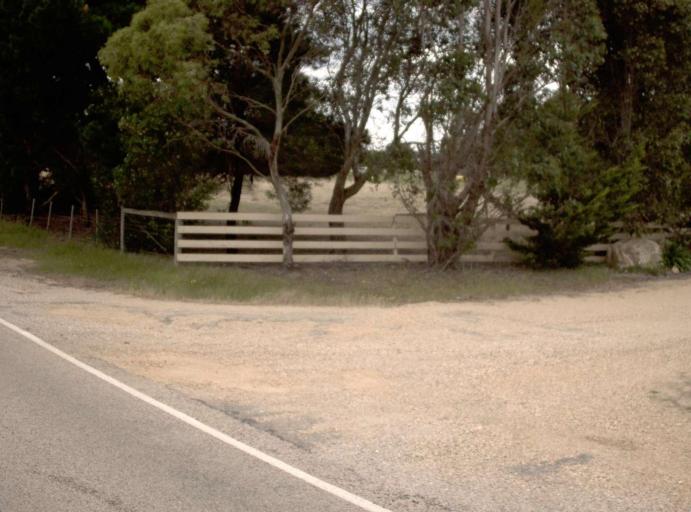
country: AU
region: Victoria
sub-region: East Gippsland
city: Bairnsdale
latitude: -37.8581
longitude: 147.5639
